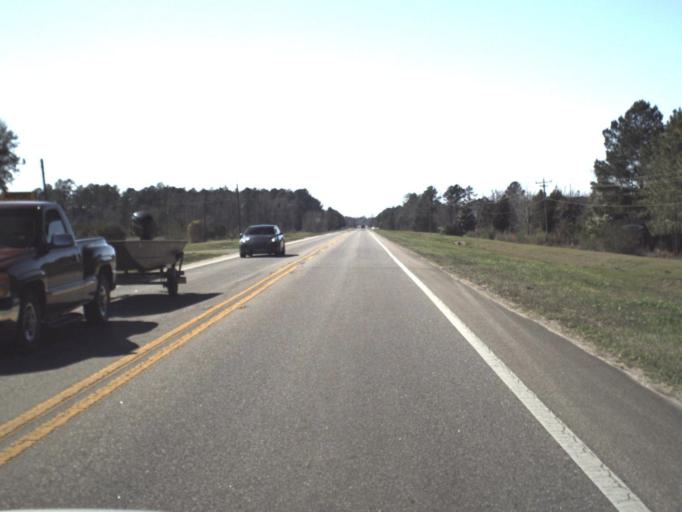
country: US
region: Florida
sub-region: Calhoun County
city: Blountstown
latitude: 30.4432
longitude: -85.0234
